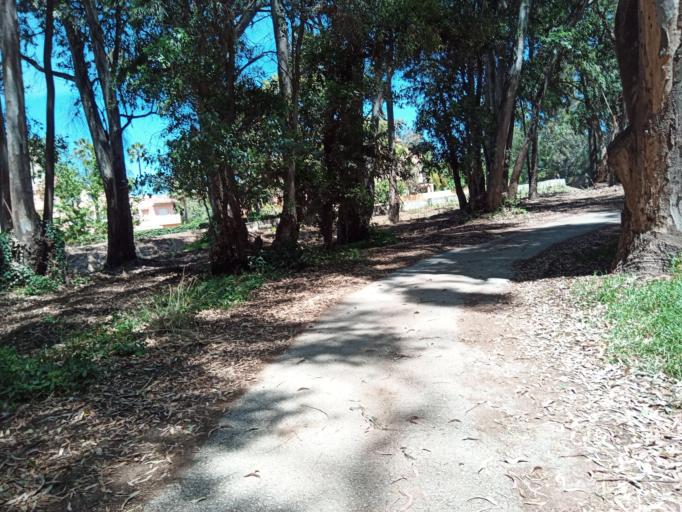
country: ES
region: Andalusia
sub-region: Provincia de Malaga
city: Ojen
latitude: 36.4884
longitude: -4.7526
